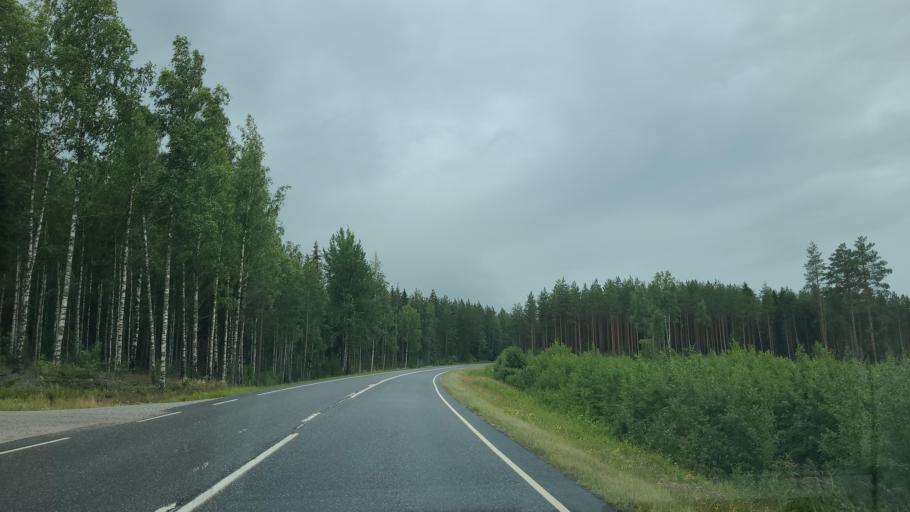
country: FI
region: Varsinais-Suomi
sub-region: Turku
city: Sauvo
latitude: 60.3270
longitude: 22.7141
